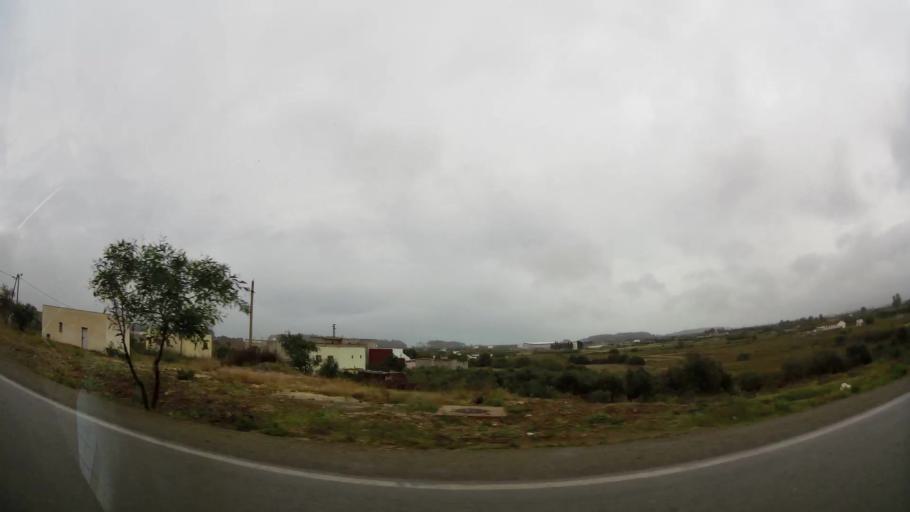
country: MA
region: Taza-Al Hoceima-Taounate
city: Imzourene
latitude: 35.1912
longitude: -3.8885
